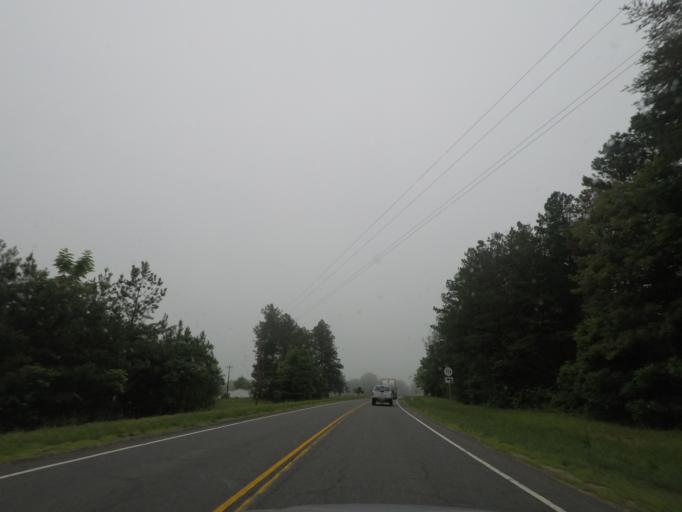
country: US
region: Virginia
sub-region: Buckingham County
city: Buckingham
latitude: 37.5100
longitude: -78.4890
